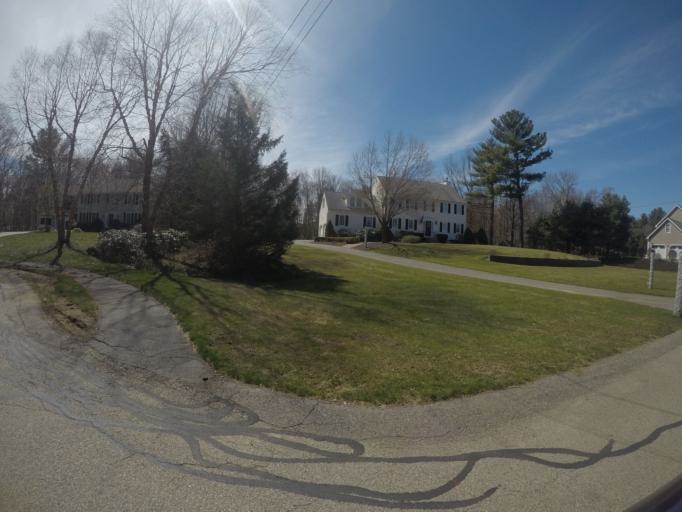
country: US
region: Massachusetts
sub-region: Bristol County
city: Easton
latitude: 42.0283
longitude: -71.0822
